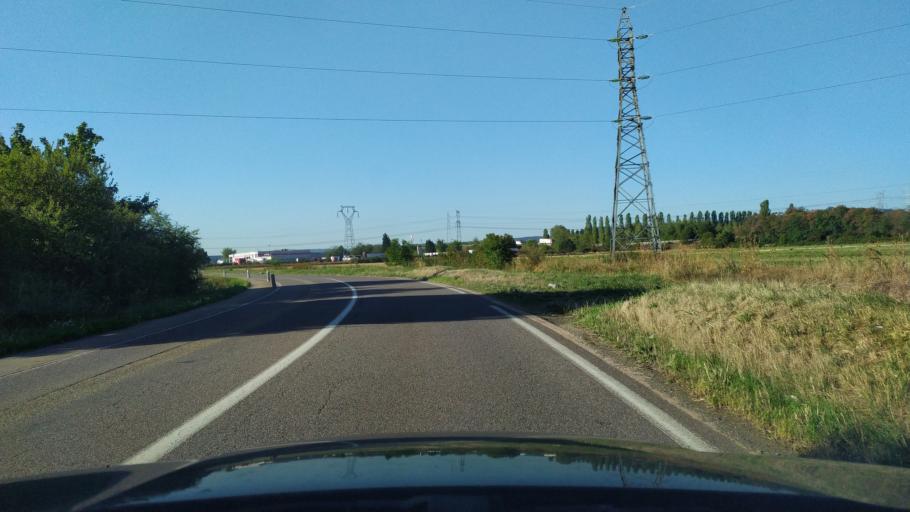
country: FR
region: Lorraine
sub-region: Departement de la Moselle
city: Maizieres-les-Metz
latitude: 49.2024
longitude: 6.1494
